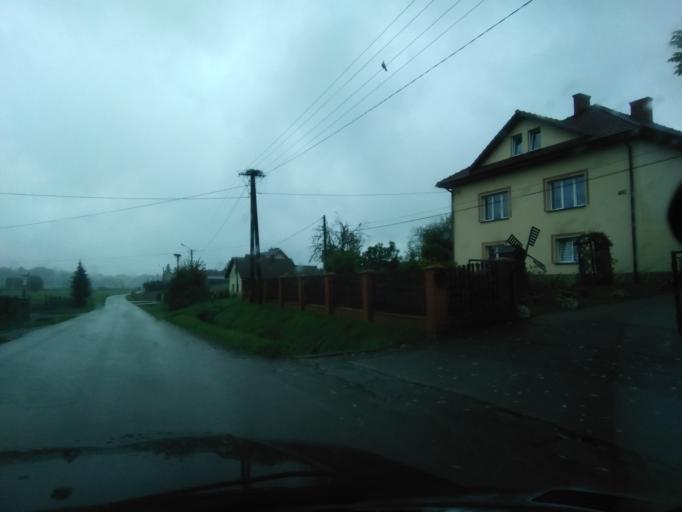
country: PL
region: Subcarpathian Voivodeship
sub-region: Powiat ropczycko-sedziszowski
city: Niedzwiada
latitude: 49.9996
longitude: 21.5521
